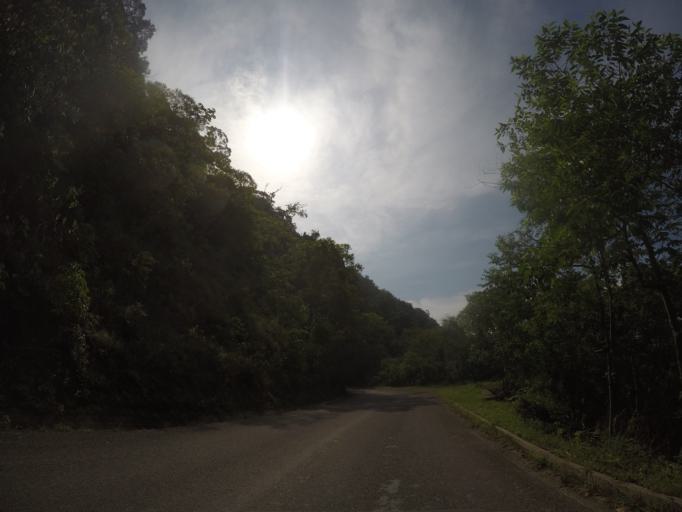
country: MX
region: Oaxaca
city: Pluma Hidalgo
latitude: 15.9415
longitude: -96.4411
